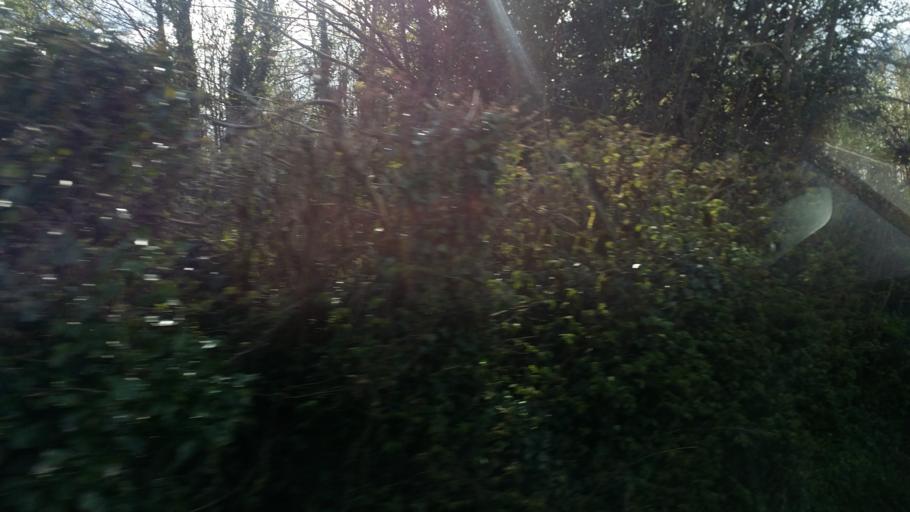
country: GB
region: Northern Ireland
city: Irvinestown
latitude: 54.4503
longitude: -7.8038
